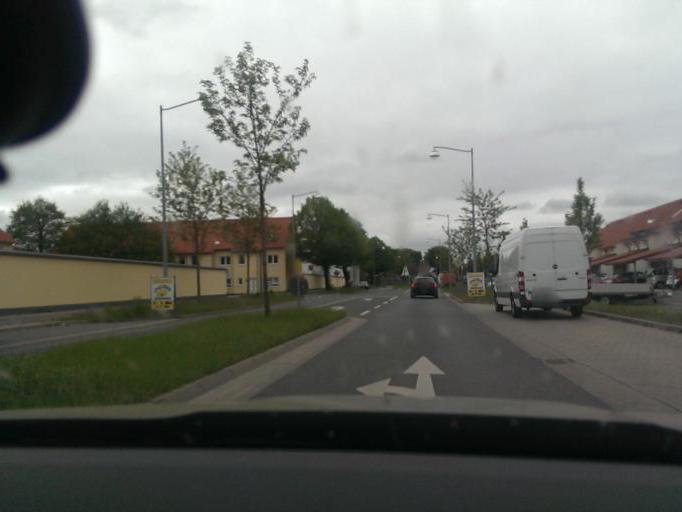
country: DE
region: Lower Saxony
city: Langenhagen
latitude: 52.4839
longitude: 9.7321
